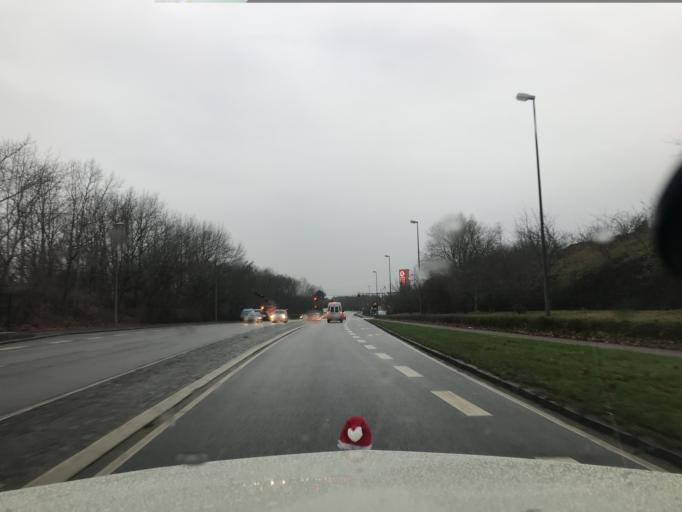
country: DK
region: South Denmark
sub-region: Sonderborg Kommune
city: Sonderborg
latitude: 54.9208
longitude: 9.7841
